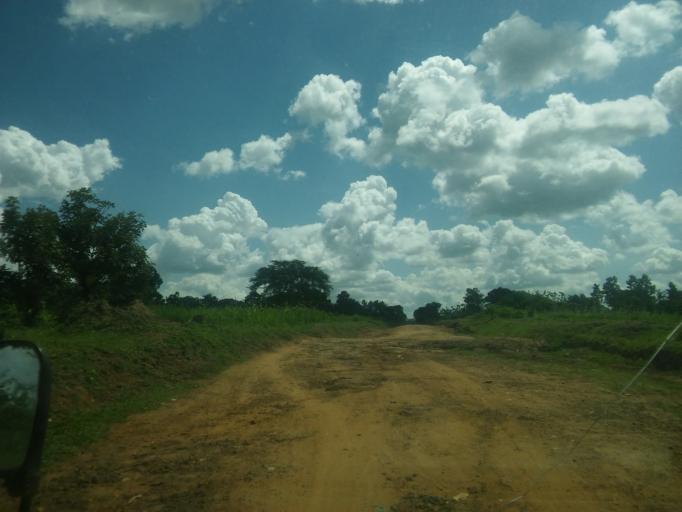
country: UG
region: Eastern Region
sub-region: Pallisa District
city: Pallisa
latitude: 1.1505
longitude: 33.8145
